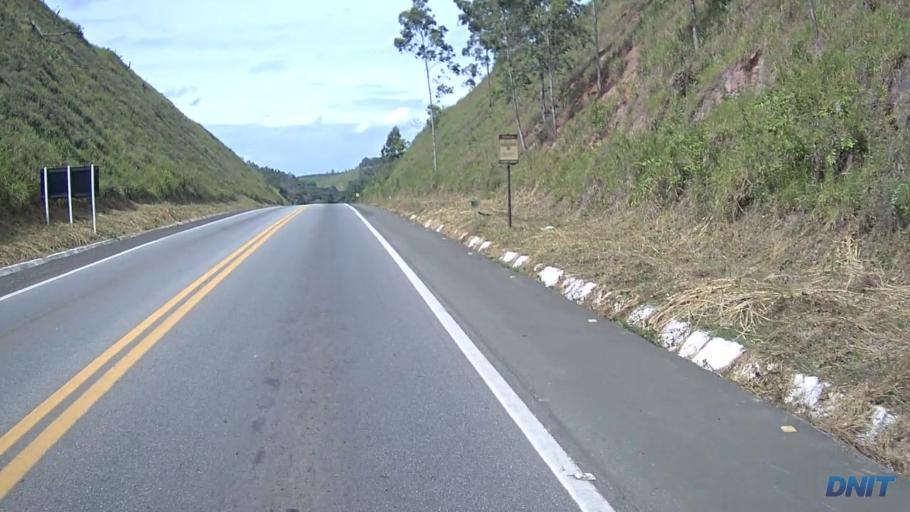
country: BR
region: Minas Gerais
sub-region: Ipatinga
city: Ipatinga
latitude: -19.4345
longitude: -42.5084
